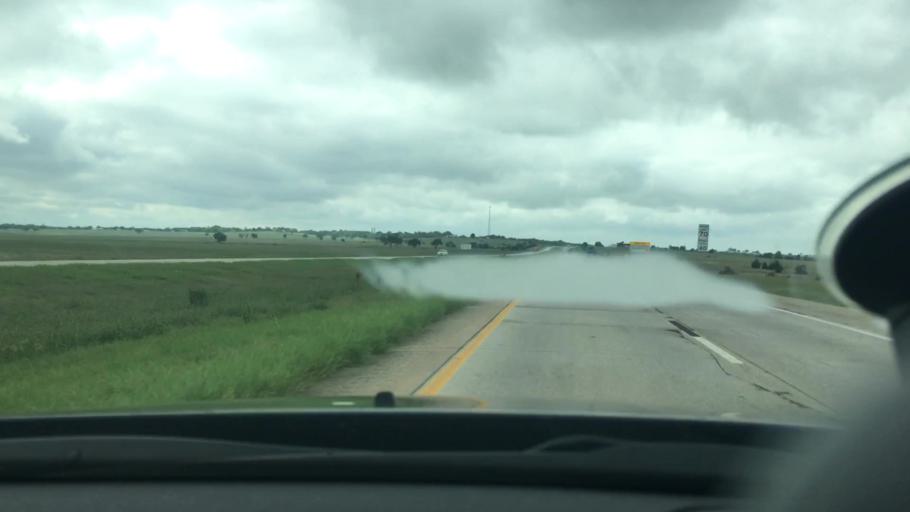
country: US
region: Oklahoma
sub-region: Bryan County
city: Durant
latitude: 34.1566
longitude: -96.2600
